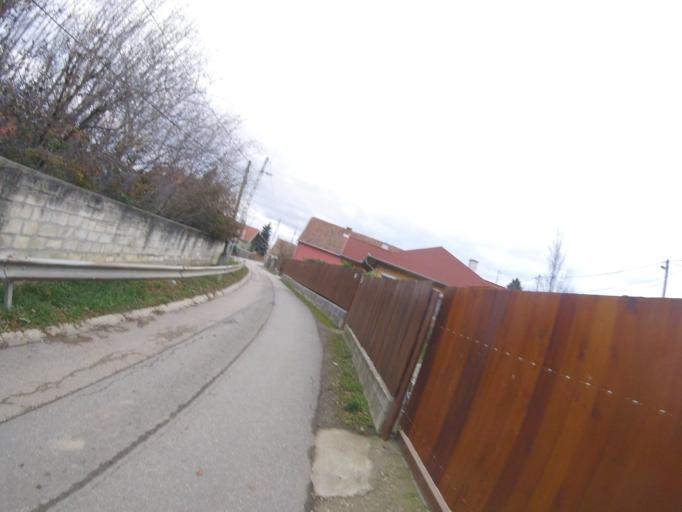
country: HU
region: Pest
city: Nagykovacsi
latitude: 47.6473
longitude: 19.0100
